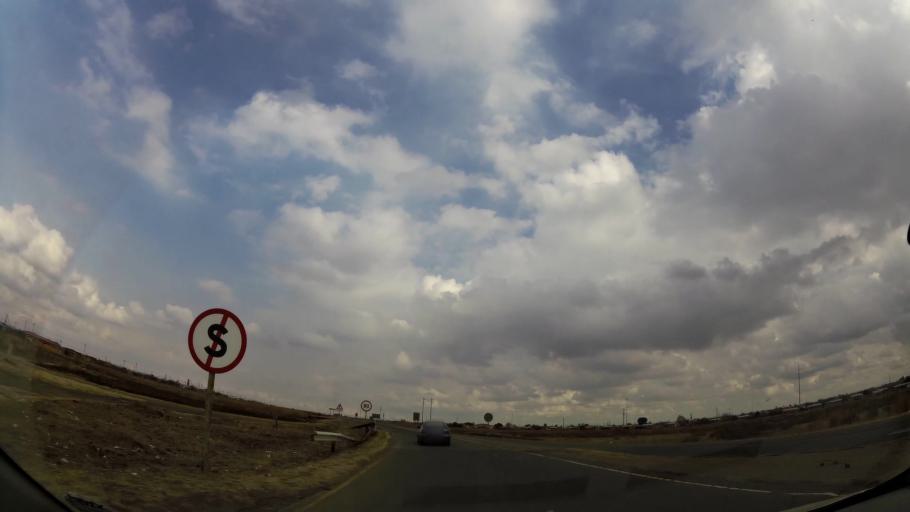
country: ZA
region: Orange Free State
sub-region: Fezile Dabi District Municipality
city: Sasolburg
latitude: -26.8471
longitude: 27.8896
